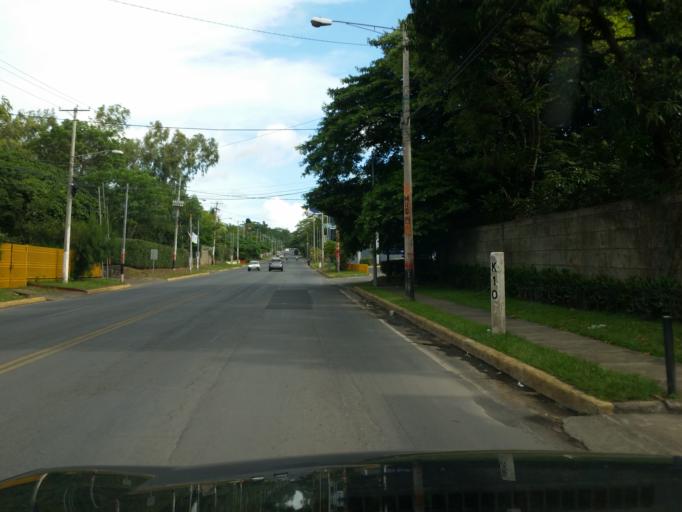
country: NI
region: Managua
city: Ciudad Sandino
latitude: 12.0923
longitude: -86.3240
